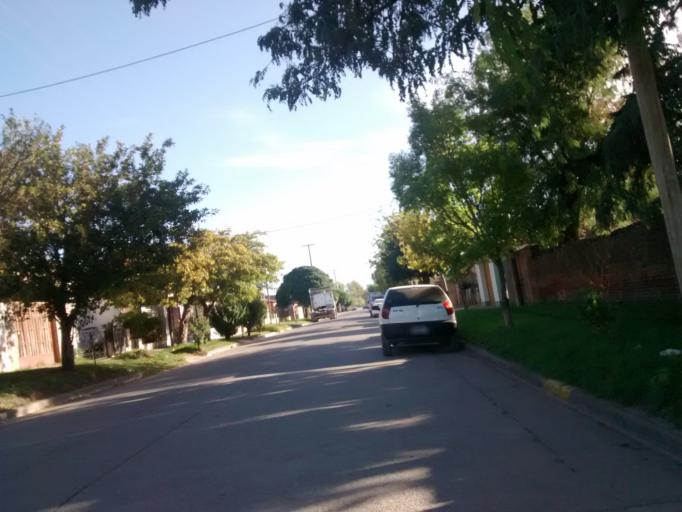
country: AR
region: Buenos Aires
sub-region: Partido de Loberia
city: Loberia
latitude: -38.1690
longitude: -58.7805
